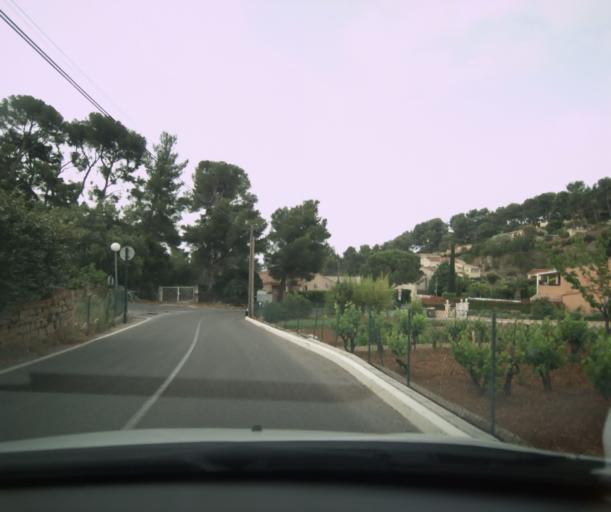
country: FR
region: Provence-Alpes-Cote d'Azur
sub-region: Departement du Var
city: Carqueiranne
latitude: 43.1006
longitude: 6.0801
